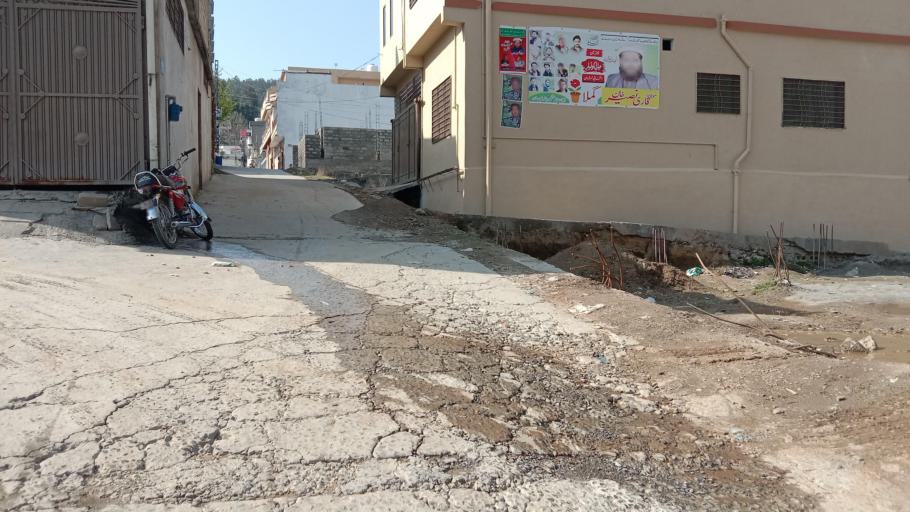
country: PK
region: Khyber Pakhtunkhwa
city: Abbottabad
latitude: 34.1757
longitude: 73.2144
